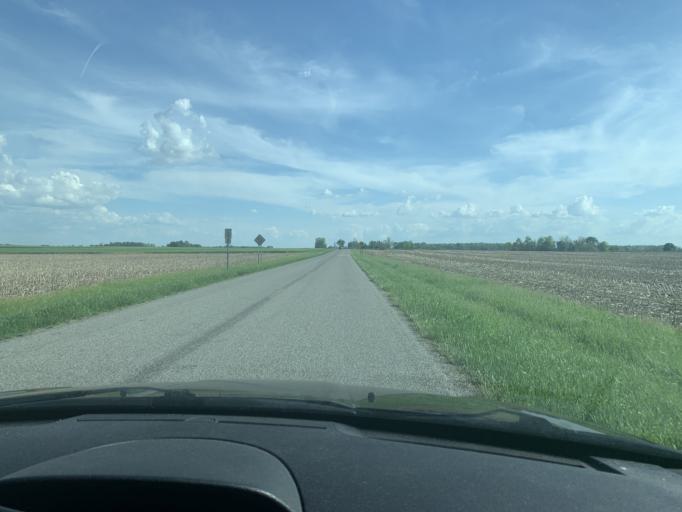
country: US
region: Ohio
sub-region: Logan County
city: De Graff
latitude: 40.2979
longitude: -84.0124
